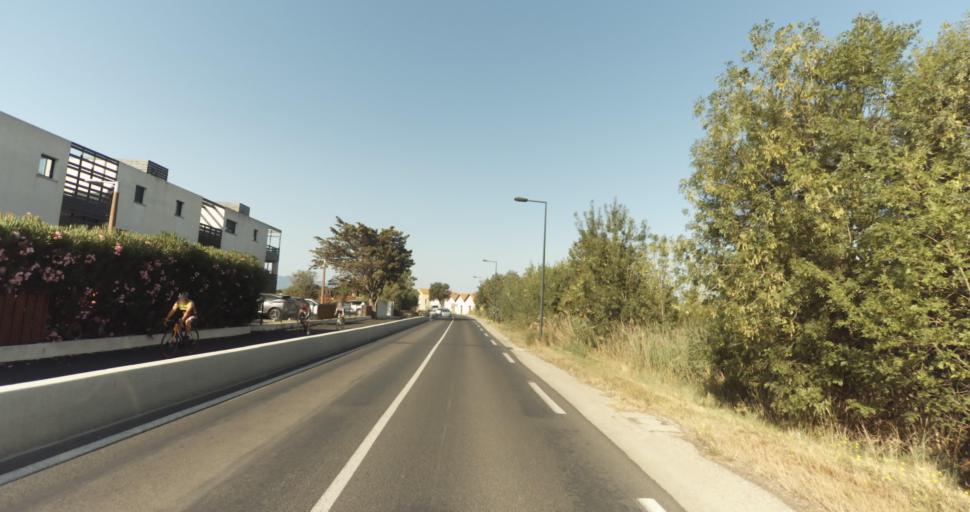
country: FR
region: Languedoc-Roussillon
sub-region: Departement des Pyrenees-Orientales
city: Saint-Cyprien-Plage
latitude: 42.6382
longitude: 3.0151
